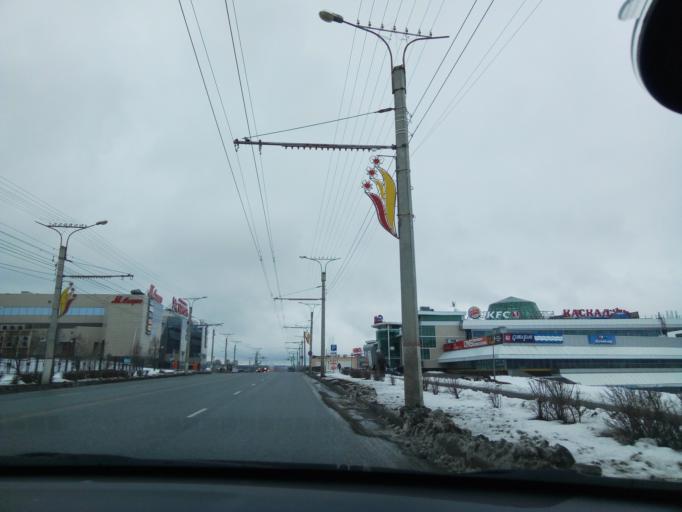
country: RU
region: Chuvashia
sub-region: Cheboksarskiy Rayon
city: Cheboksary
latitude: 56.1367
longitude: 47.2423
